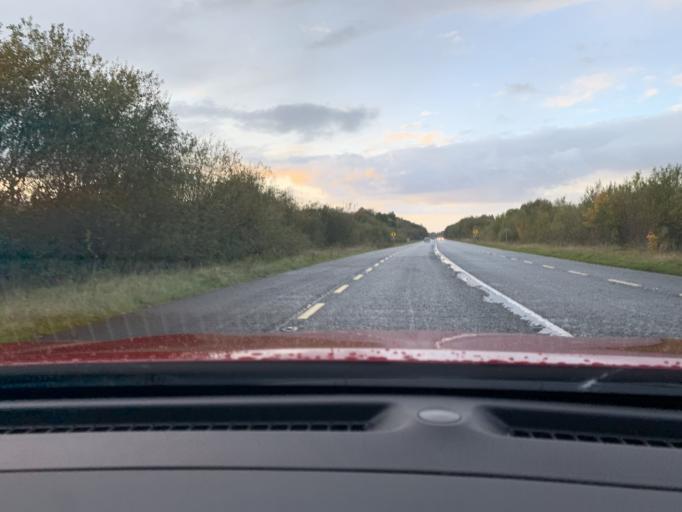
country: IE
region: Connaught
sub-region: County Leitrim
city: Carrick-on-Shannon
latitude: 53.9505
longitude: -8.1496
